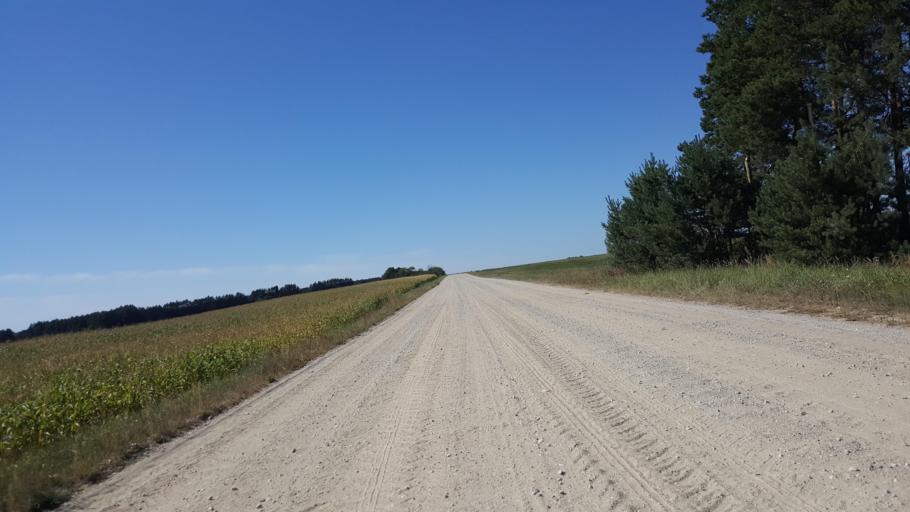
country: PL
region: Lublin Voivodeship
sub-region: Powiat bialski
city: Rokitno
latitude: 52.2268
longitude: 23.3330
